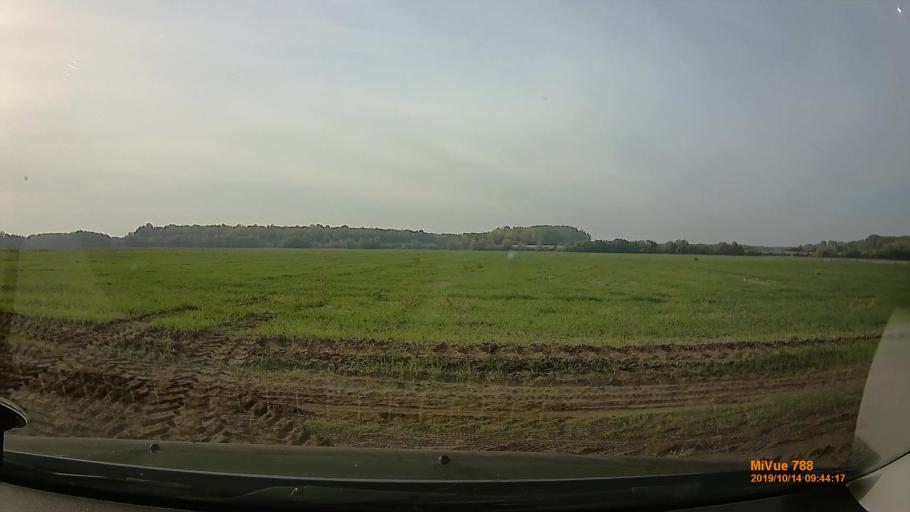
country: HU
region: Pest
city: Pilis
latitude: 47.2944
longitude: 19.5258
